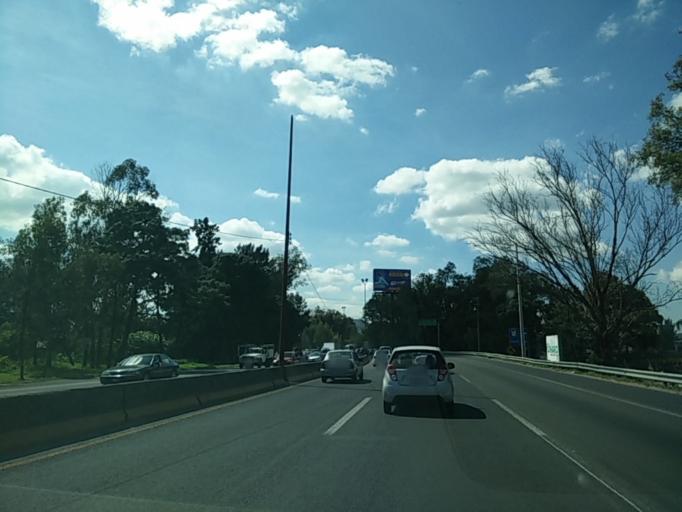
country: MX
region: Jalisco
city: Zapopan2
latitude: 20.7083
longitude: -103.4444
